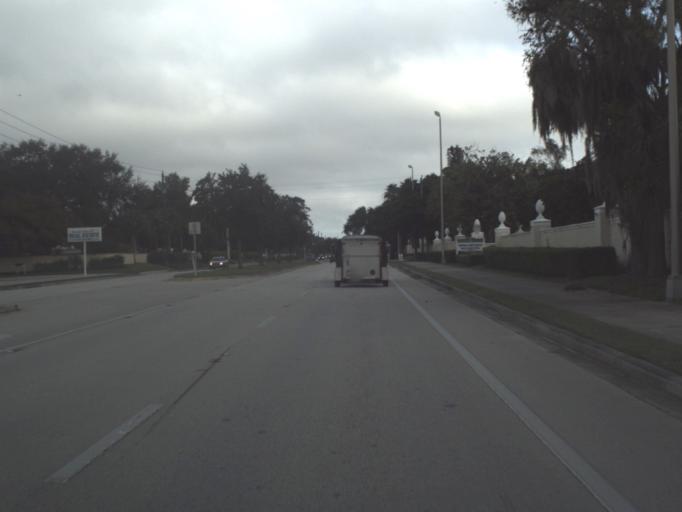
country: US
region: Florida
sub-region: Sarasota County
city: Englewood
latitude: 26.9948
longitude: -82.3717
